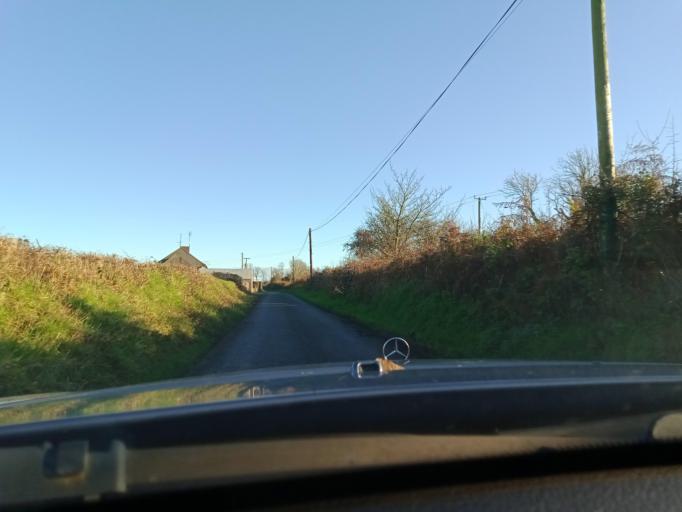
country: IE
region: Leinster
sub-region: Kilkenny
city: Mooncoin
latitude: 52.3015
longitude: -7.1990
